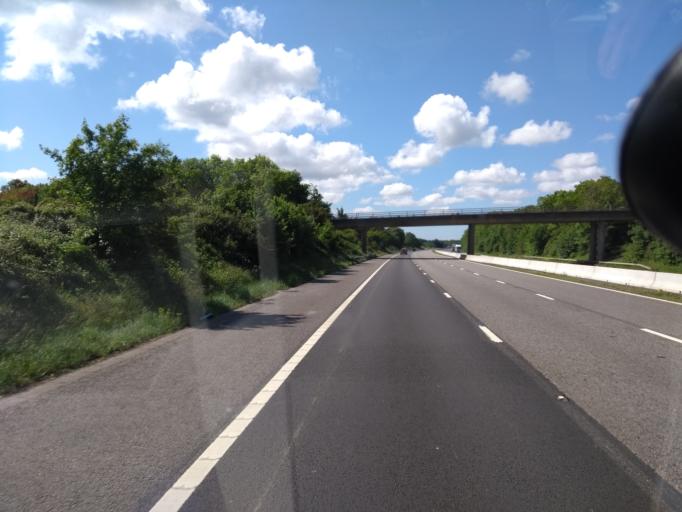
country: GB
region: England
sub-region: Somerset
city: North Petherton
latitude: 51.0832
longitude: -3.0062
